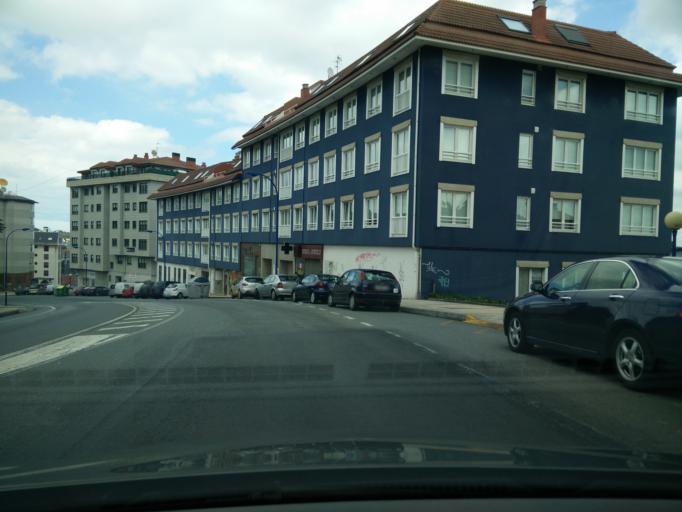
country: ES
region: Galicia
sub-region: Provincia da Coruna
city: Culleredo
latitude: 43.3231
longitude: -8.3834
